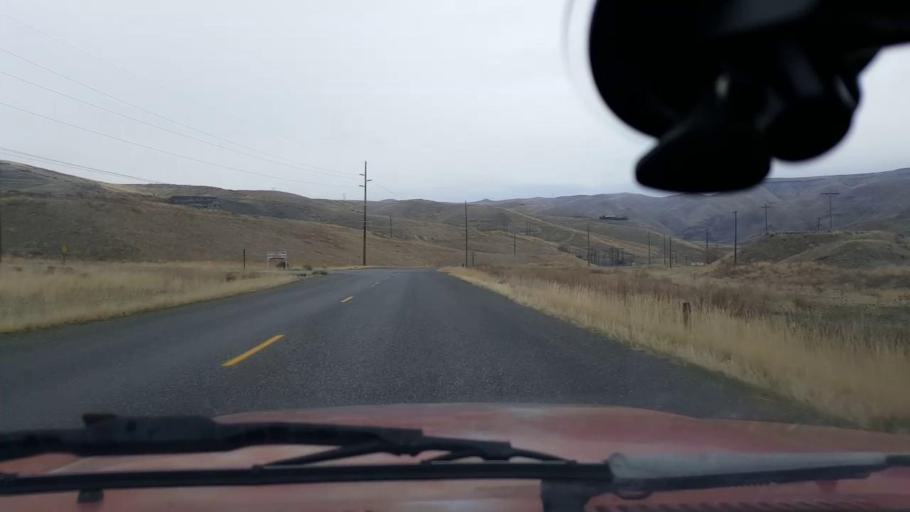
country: US
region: Washington
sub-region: Asotin County
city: Clarkston Heights-Vineland
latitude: 46.4081
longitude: -117.1077
